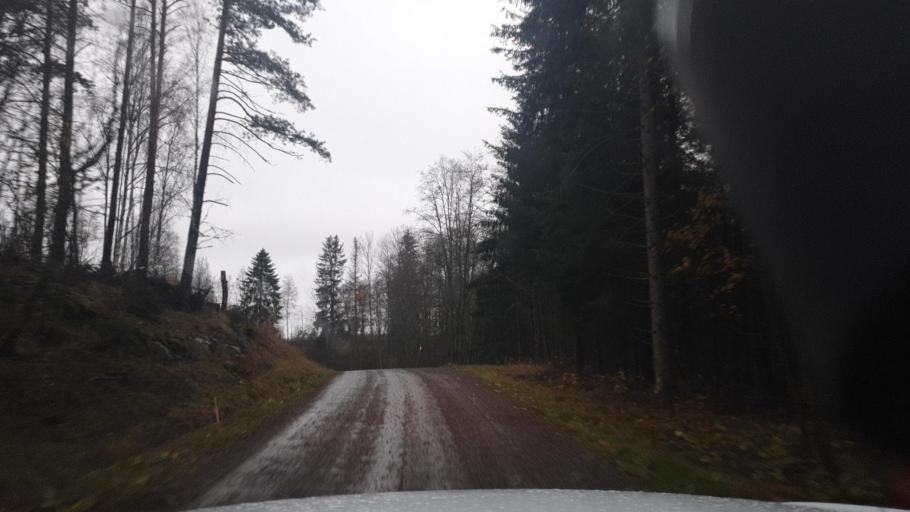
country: SE
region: Vaermland
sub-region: Eda Kommun
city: Charlottenberg
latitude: 59.7321
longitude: 12.1469
